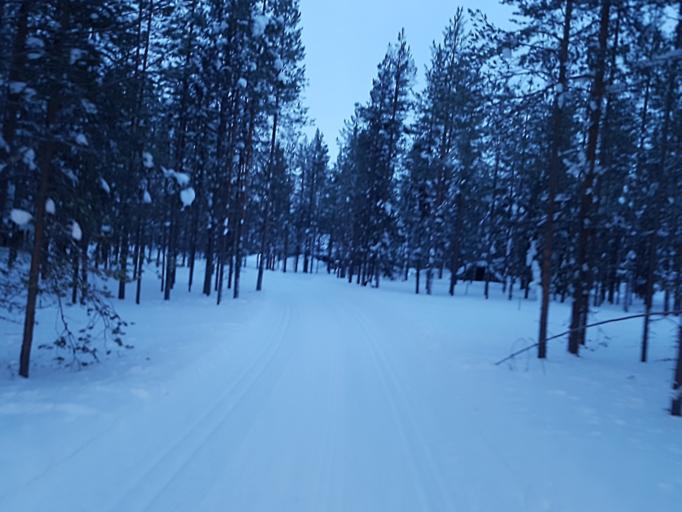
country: FI
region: Lapland
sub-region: Tunturi-Lappi
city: Kolari
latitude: 67.6233
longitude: 24.1572
